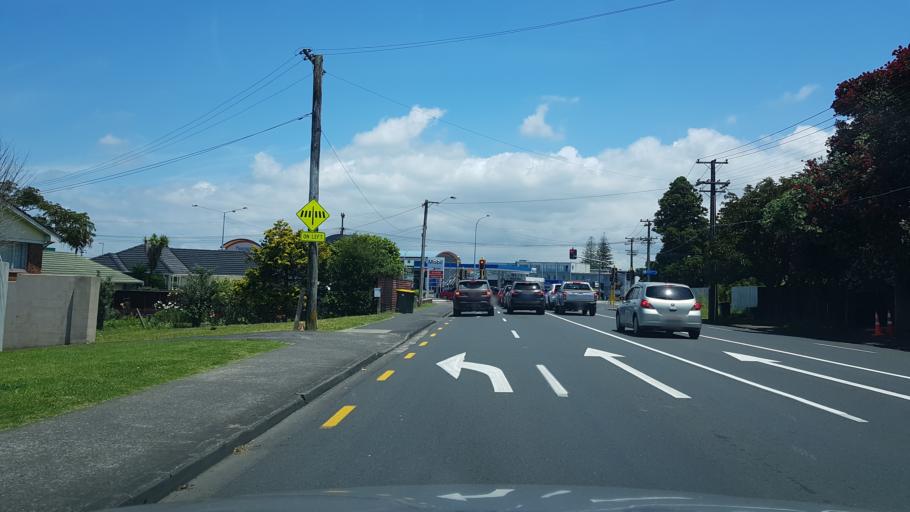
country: NZ
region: Auckland
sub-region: Auckland
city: North Shore
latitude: -36.7896
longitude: 174.7659
